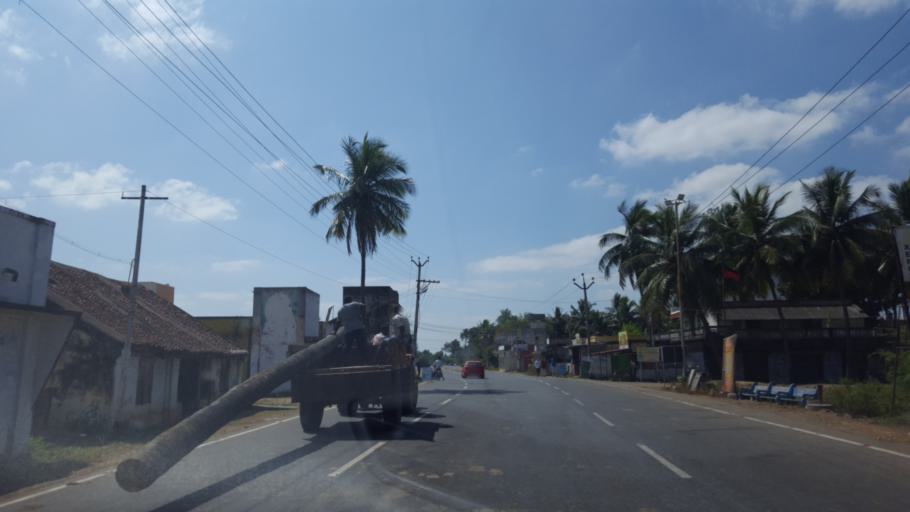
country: IN
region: Tamil Nadu
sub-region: Kancheepuram
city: Mamallapuram
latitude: 12.6481
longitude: 80.1744
